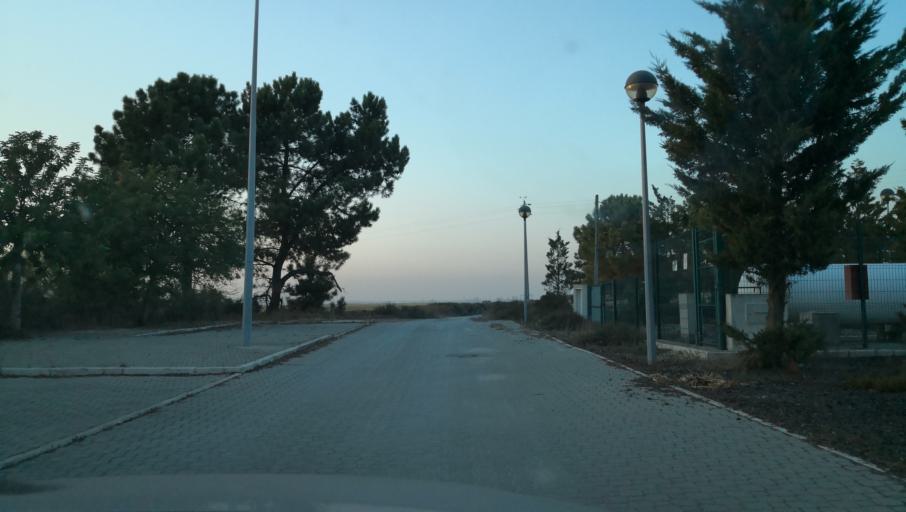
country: PT
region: Setubal
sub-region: Setubal
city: Setubal
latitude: 38.3990
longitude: -8.7731
